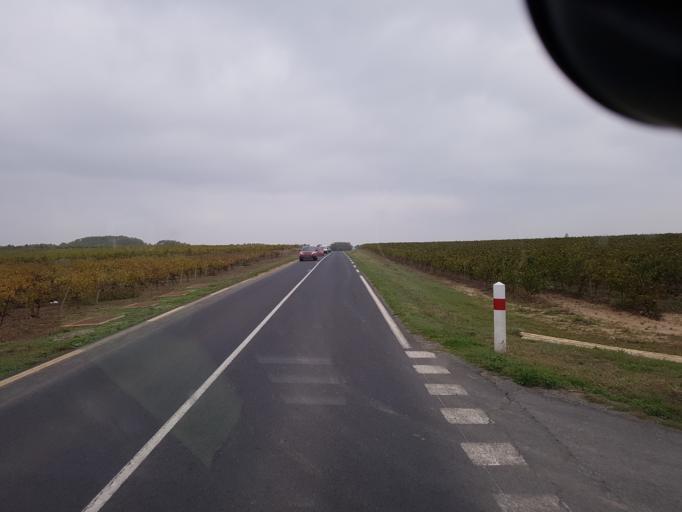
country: FR
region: Languedoc-Roussillon
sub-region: Departement de l'Herault
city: Pinet
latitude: 43.3980
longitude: 3.5388
